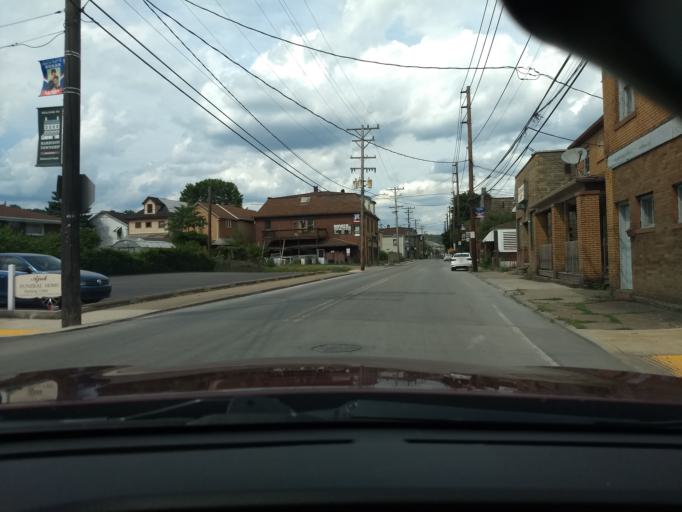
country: US
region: Pennsylvania
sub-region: Allegheny County
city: Brackenridge
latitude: 40.6102
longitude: -79.7222
